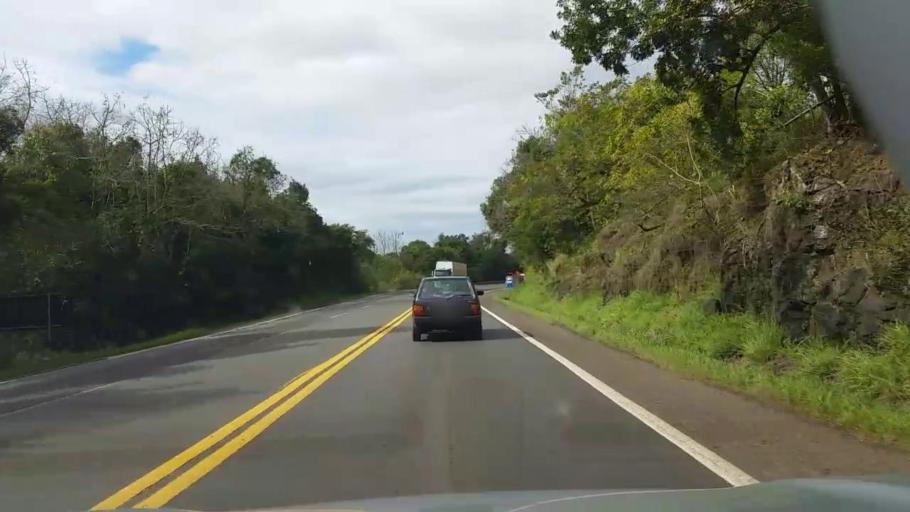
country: BR
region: Rio Grande do Sul
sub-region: Arroio Do Meio
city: Arroio do Meio
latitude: -29.3877
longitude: -52.0460
